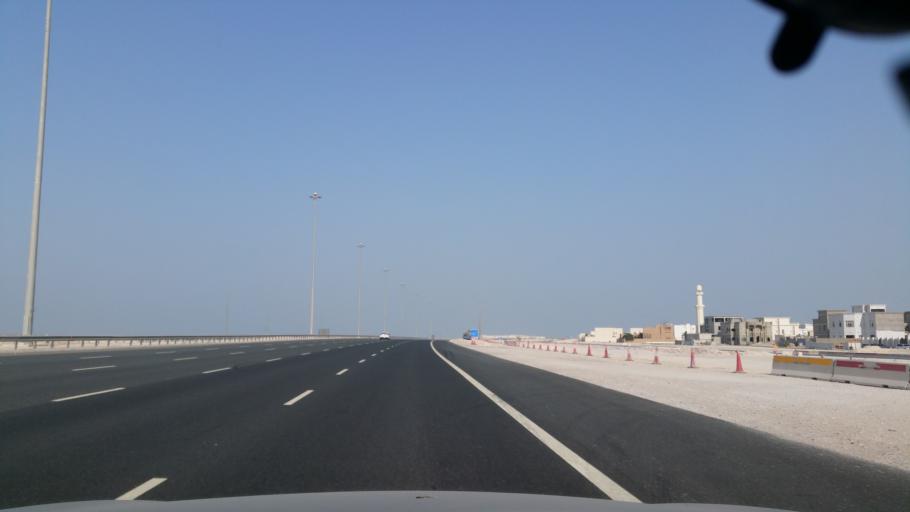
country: QA
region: Baladiyat Umm Salal
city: Umm Salal `Ali
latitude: 25.4551
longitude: 51.4364
